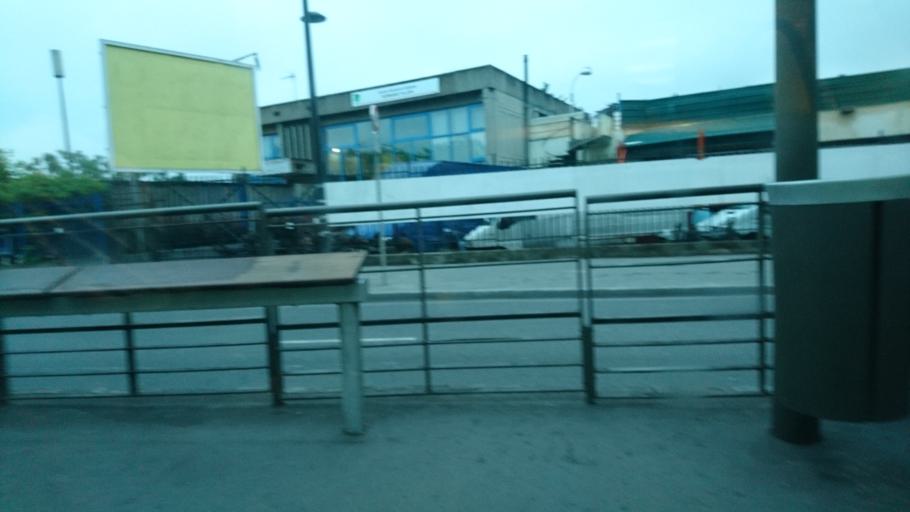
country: FR
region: Ile-de-France
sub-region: Departement de Seine-Saint-Denis
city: Pierrefitte-sur-Seine
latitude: 48.9555
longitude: 2.3581
